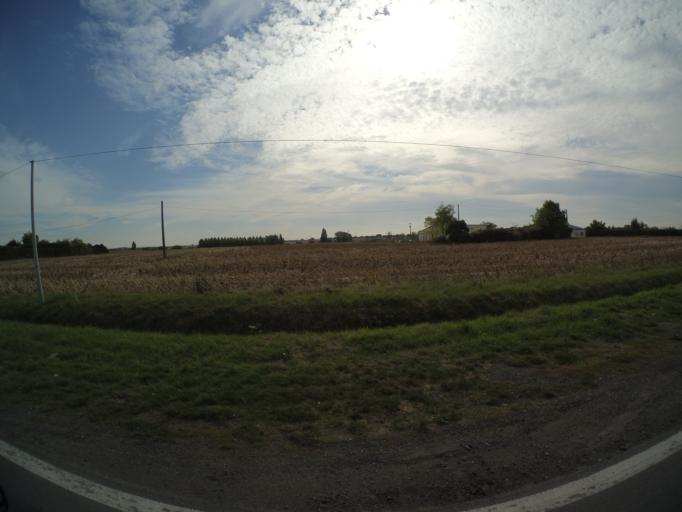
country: FR
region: Pays de la Loire
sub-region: Departement de Maine-et-Loire
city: Distre
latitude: 47.2139
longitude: -0.1755
